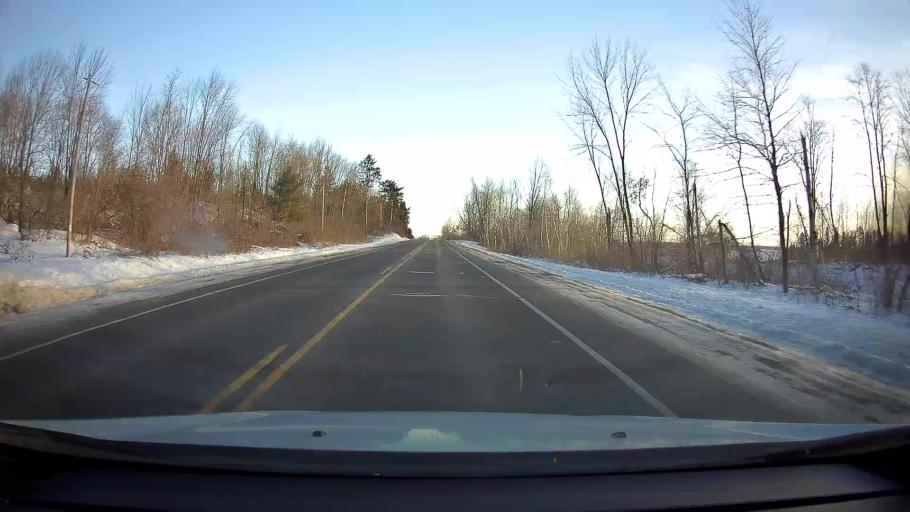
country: US
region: Wisconsin
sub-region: Barron County
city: Turtle Lake
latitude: 45.4681
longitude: -92.0887
